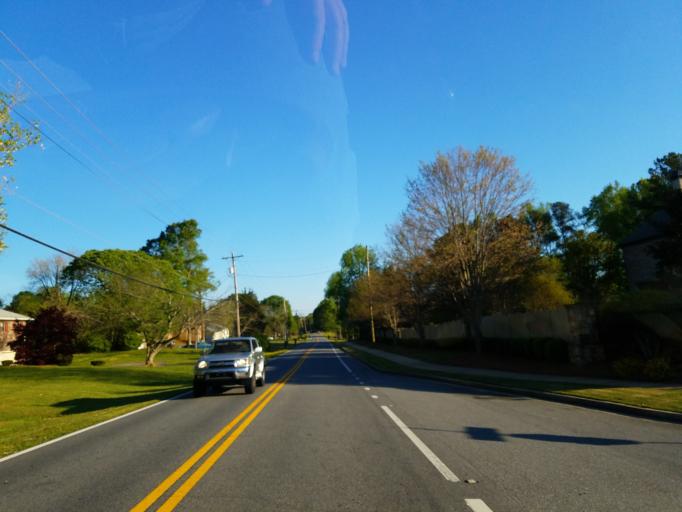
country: US
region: Georgia
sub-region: Cobb County
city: Kennesaw
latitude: 33.9439
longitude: -84.6422
